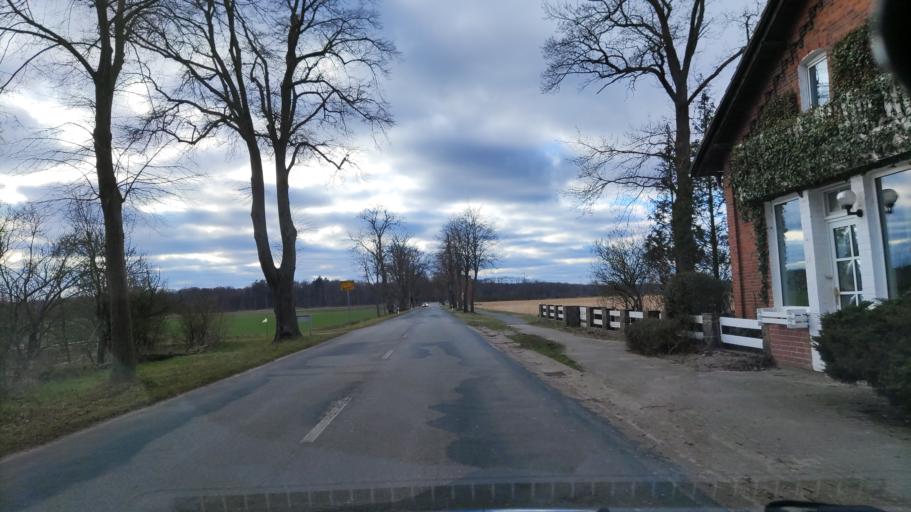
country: DE
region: Lower Saxony
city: Klein Gusborn
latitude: 53.1053
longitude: 11.1902
